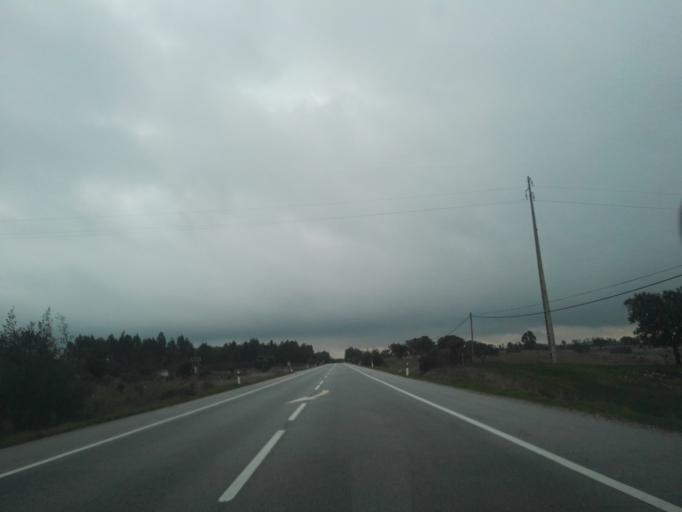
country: PT
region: Portalegre
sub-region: Portalegre
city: Urra
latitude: 39.2320
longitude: -7.3870
